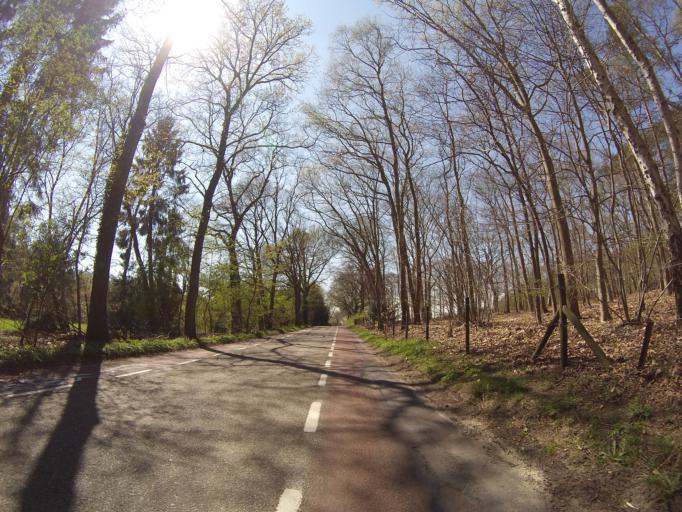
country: NL
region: Utrecht
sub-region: Gemeente Utrechtse Heuvelrug
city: Amerongen
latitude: 52.0101
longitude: 5.4700
